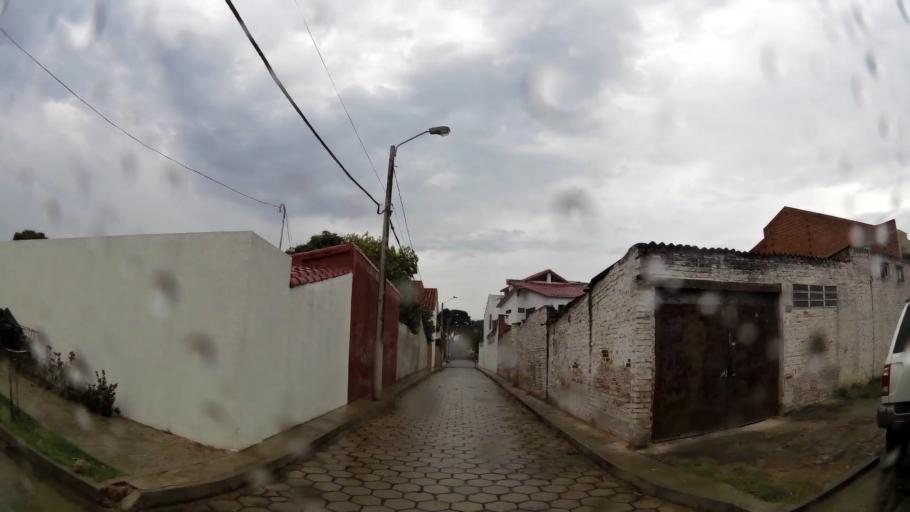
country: BO
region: Santa Cruz
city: Santa Cruz de la Sierra
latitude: -17.8032
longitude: -63.1554
